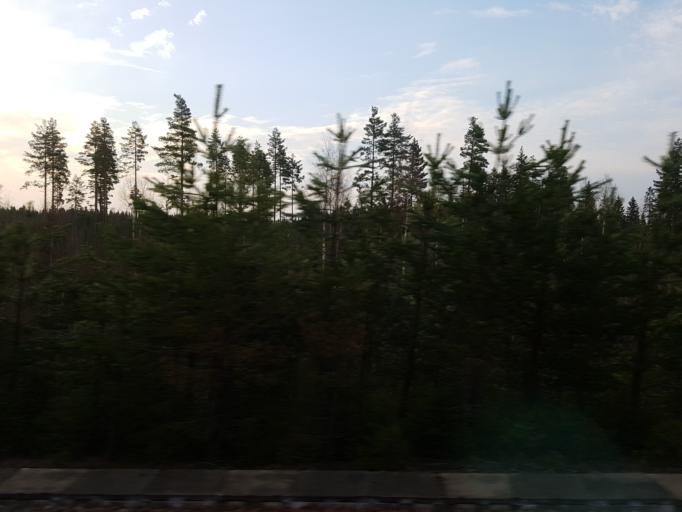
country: NO
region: Akershus
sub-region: Eidsvoll
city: Raholt
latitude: 60.2619
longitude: 11.1387
